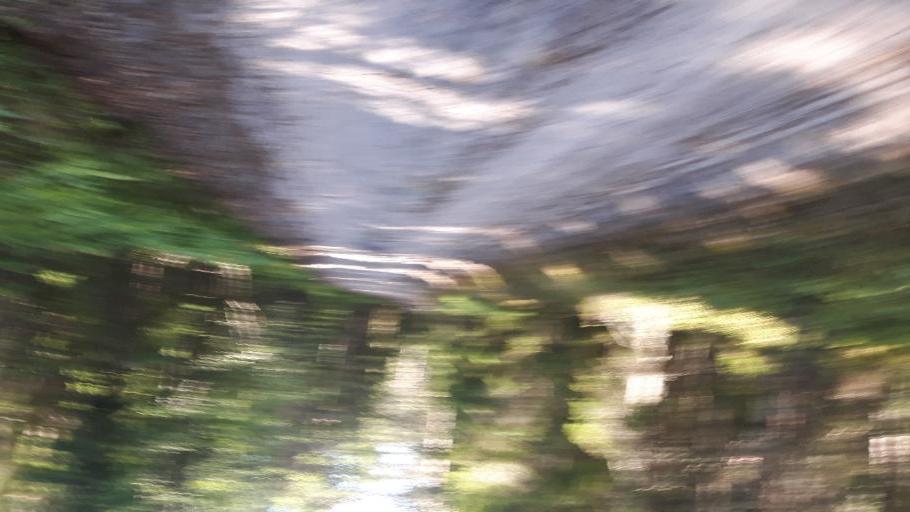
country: LV
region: Salacgrivas
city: Salacgriva
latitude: 57.7194
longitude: 24.3476
